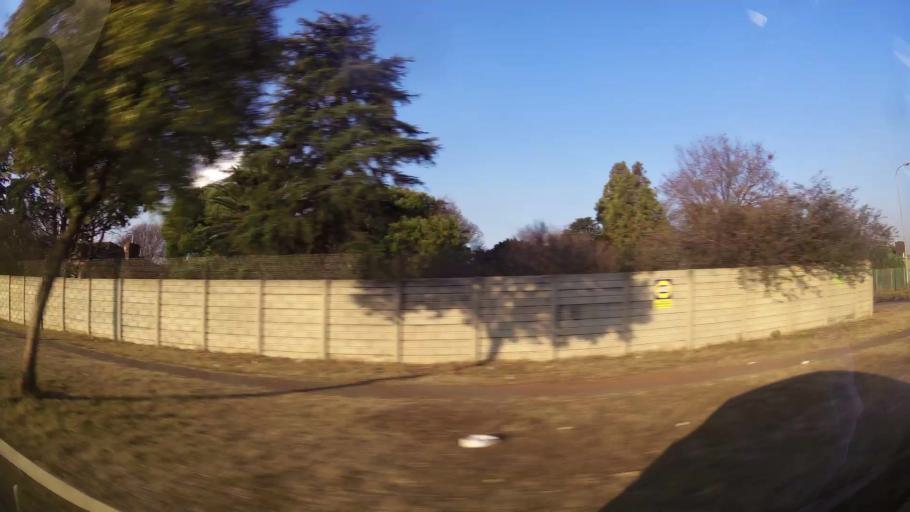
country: ZA
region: Gauteng
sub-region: Ekurhuleni Metropolitan Municipality
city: Germiston
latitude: -26.2709
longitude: 28.2251
